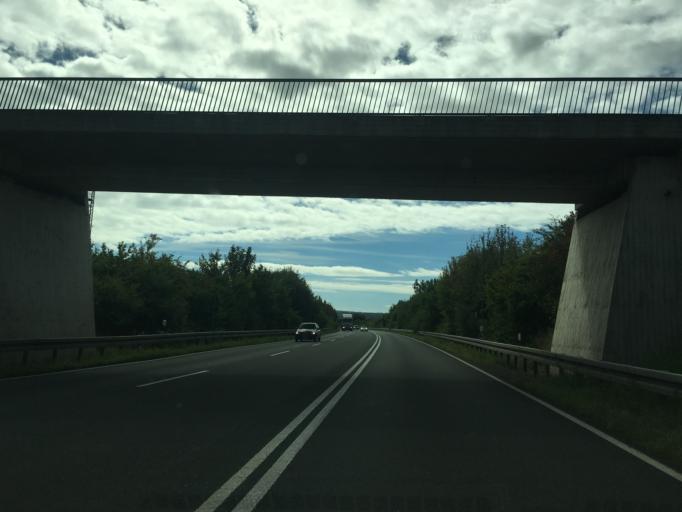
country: DE
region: Lower Saxony
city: Hessisch Oldendorf
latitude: 52.1417
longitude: 9.2906
